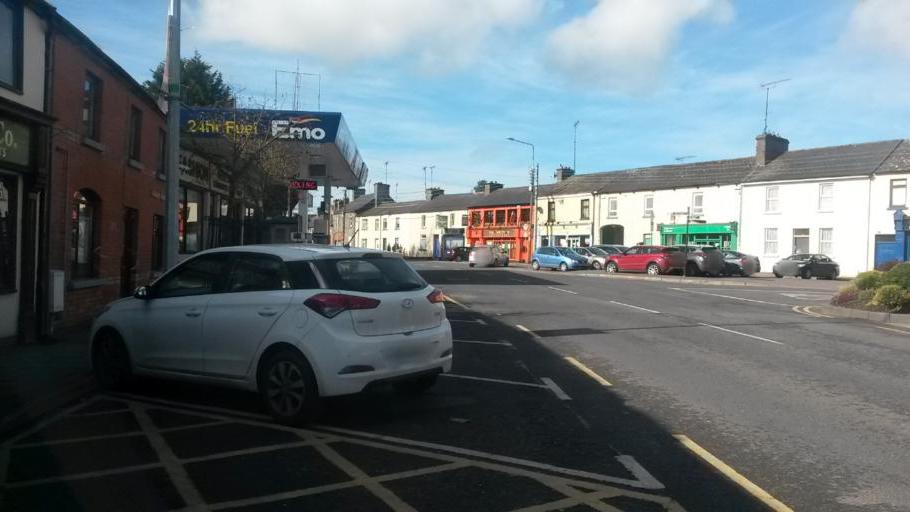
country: IE
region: Leinster
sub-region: An Mhi
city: Kells
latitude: 53.7252
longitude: -6.8796
